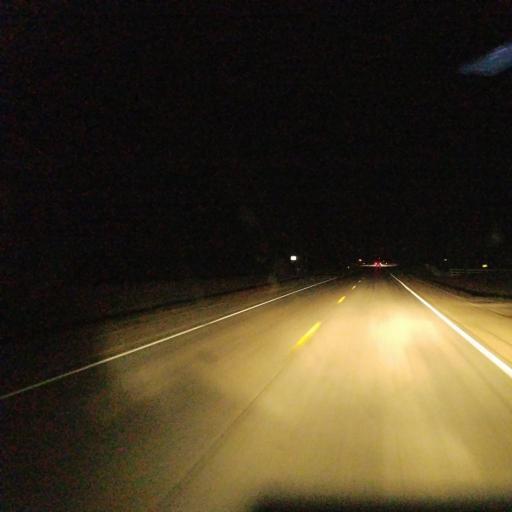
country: US
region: Illinois
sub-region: Knox County
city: Abingdon
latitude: 40.7295
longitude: -90.4546
